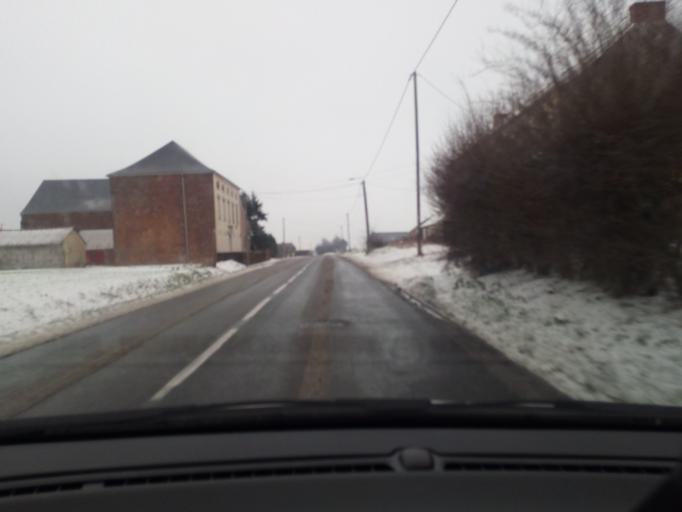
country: FR
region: Nord-Pas-de-Calais
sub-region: Departement du Nord
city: La Longueville
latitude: 50.3287
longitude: 3.8676
